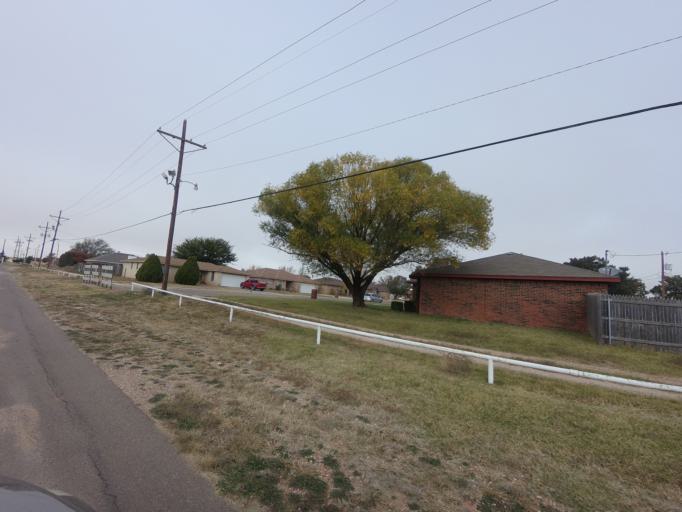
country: US
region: New Mexico
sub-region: Curry County
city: Clovis
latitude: 34.4266
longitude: -103.2294
